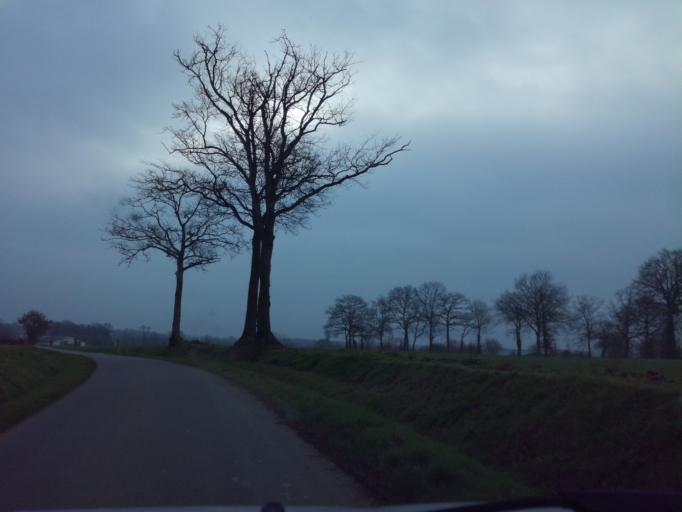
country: FR
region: Brittany
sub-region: Departement d'Ille-et-Vilaine
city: Gosne
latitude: 48.2610
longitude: -1.4638
